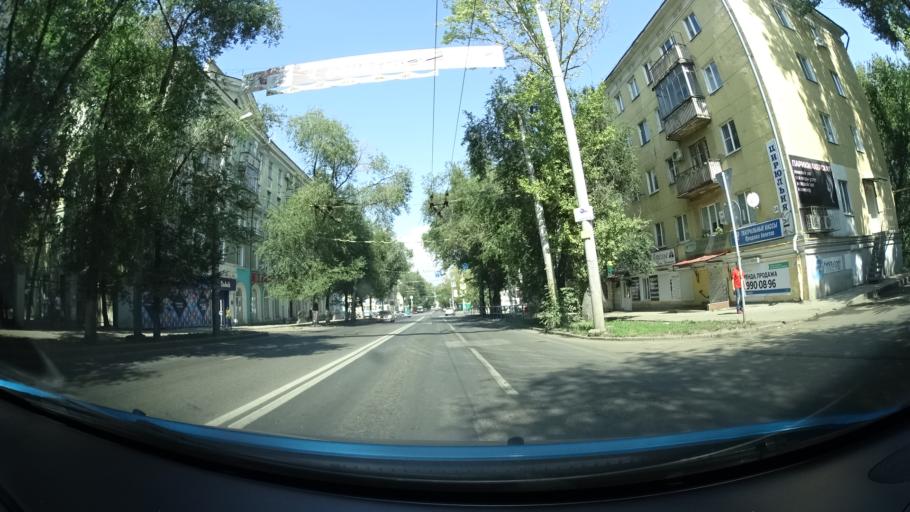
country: RU
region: Samara
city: Samara
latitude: 53.2102
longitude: 50.1570
